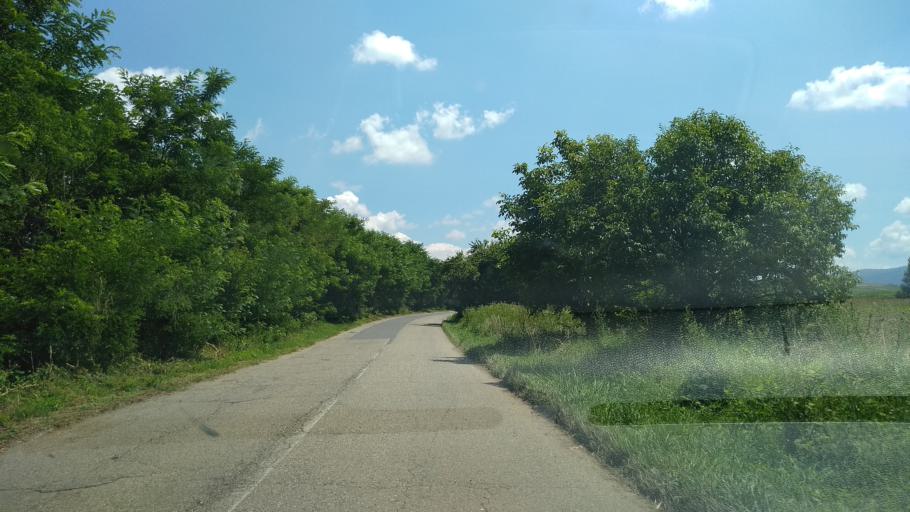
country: RO
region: Hunedoara
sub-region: Comuna Bosorod
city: Bosorod
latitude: 45.7131
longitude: 23.0420
